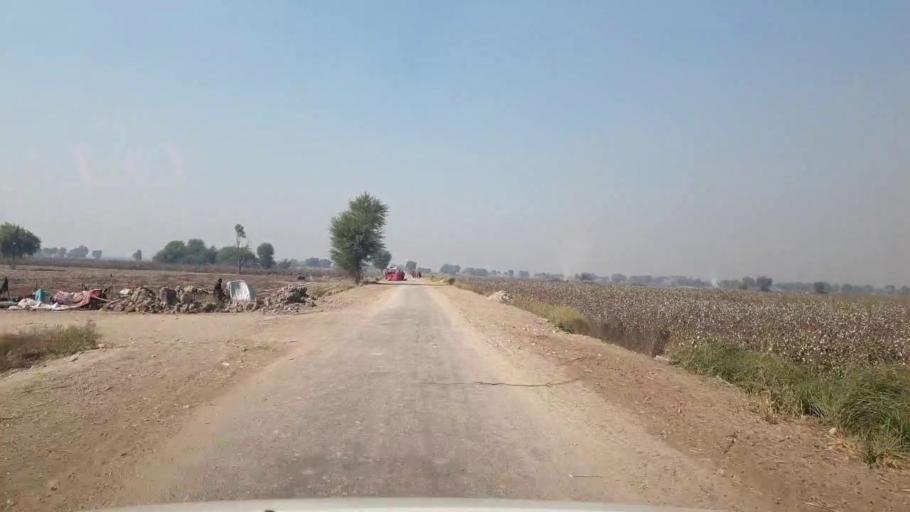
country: PK
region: Sindh
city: Bhan
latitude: 26.6117
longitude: 67.7752
